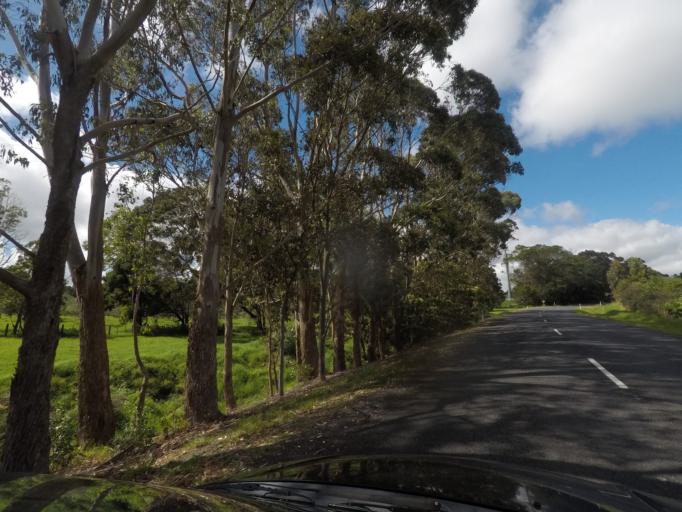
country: NZ
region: Auckland
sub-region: Auckland
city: Rothesay Bay
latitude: -36.7587
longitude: 174.6494
